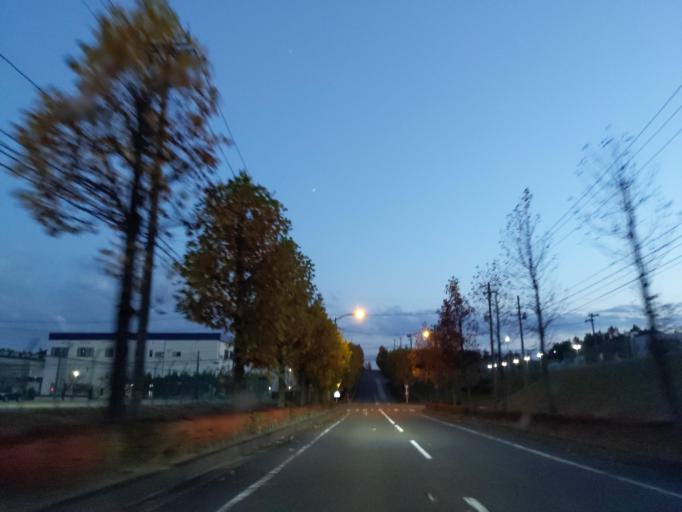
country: JP
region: Fukushima
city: Koriyama
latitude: 37.4433
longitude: 140.3060
